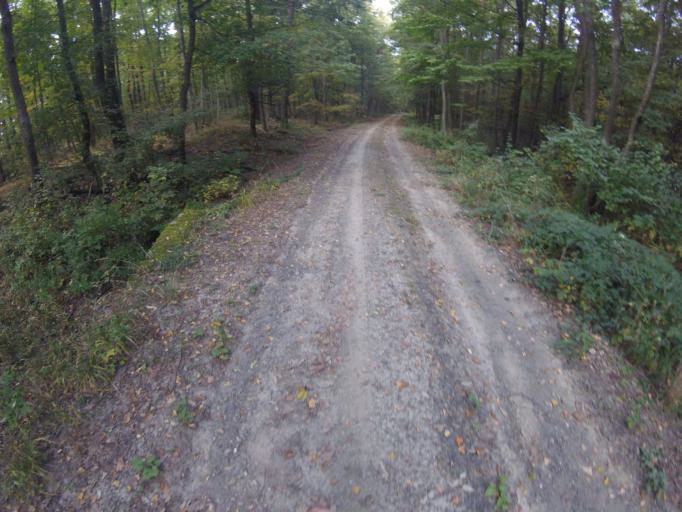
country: HU
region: Komarom-Esztergom
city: Kesztolc
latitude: 47.7737
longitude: 18.8117
